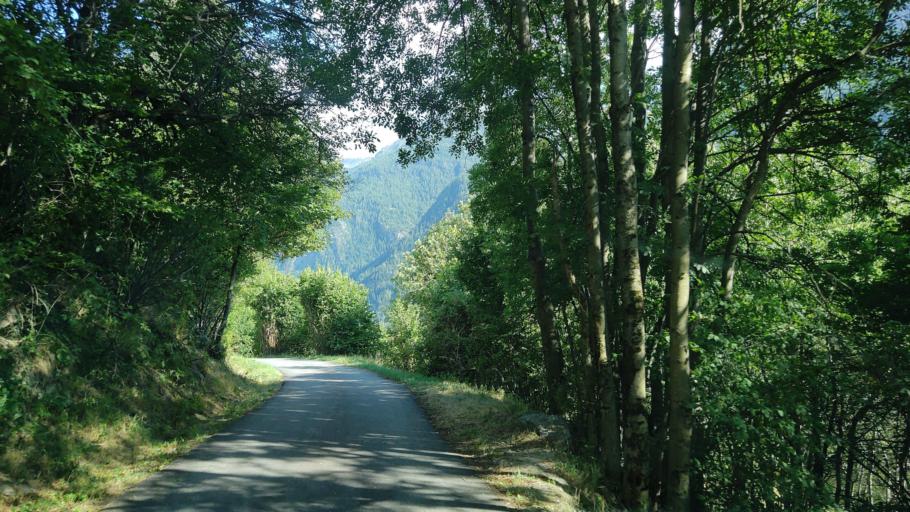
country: FR
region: Rhone-Alpes
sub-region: Departement de la Savoie
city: Val Thorens
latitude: 45.2141
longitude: 6.5604
